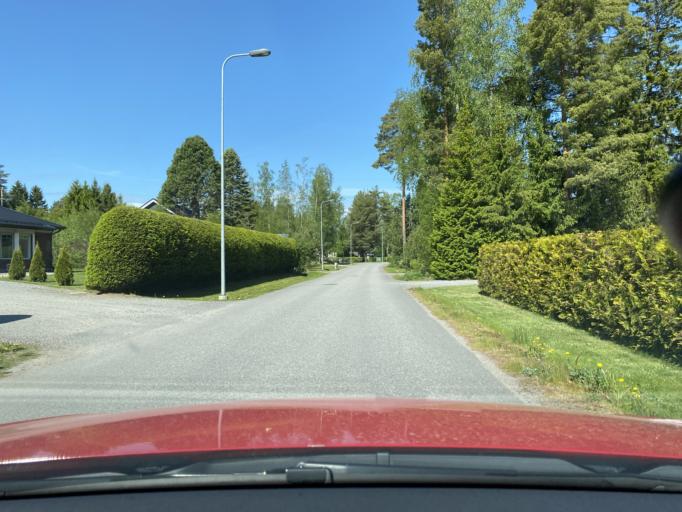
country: FI
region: Satakunta
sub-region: Rauma
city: Eura
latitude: 61.1107
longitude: 22.1352
